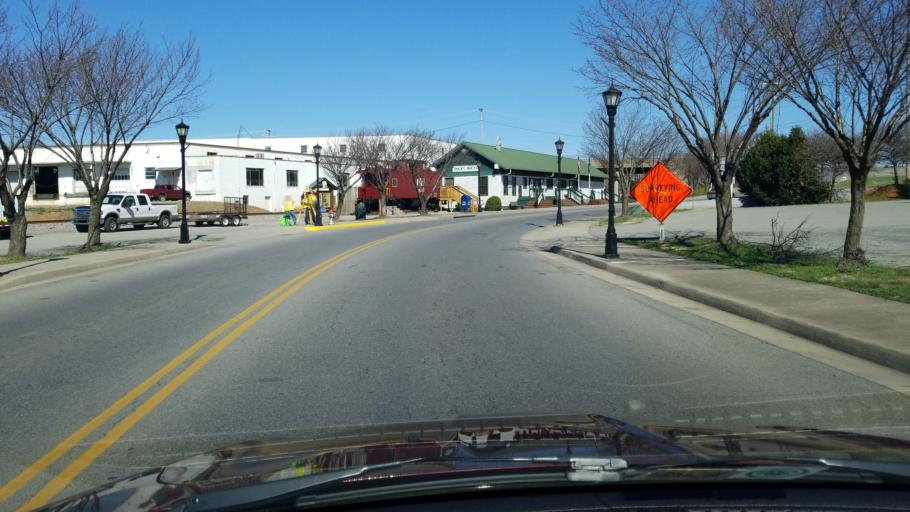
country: US
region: Virginia
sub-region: Franklin County
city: Rocky Mount
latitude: 37.0008
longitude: -79.8924
